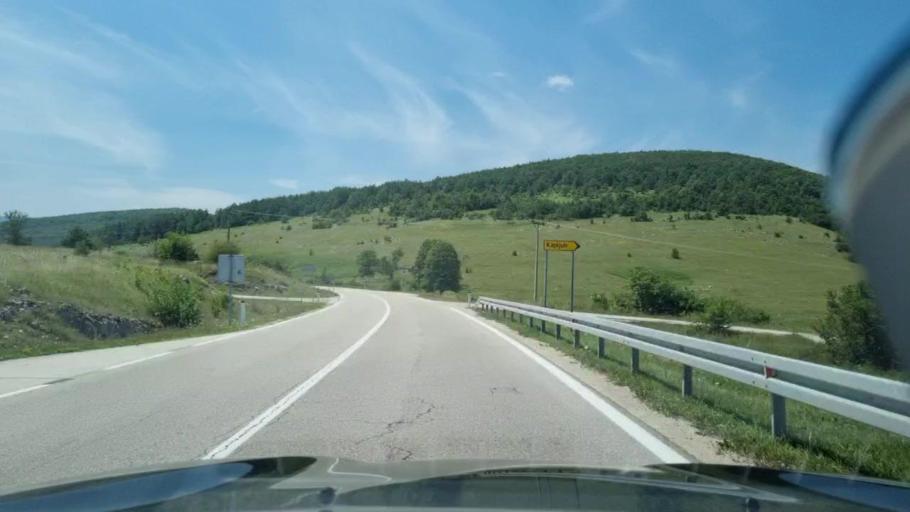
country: BA
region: Federation of Bosnia and Herzegovina
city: Sanica
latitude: 44.5651
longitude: 16.4459
